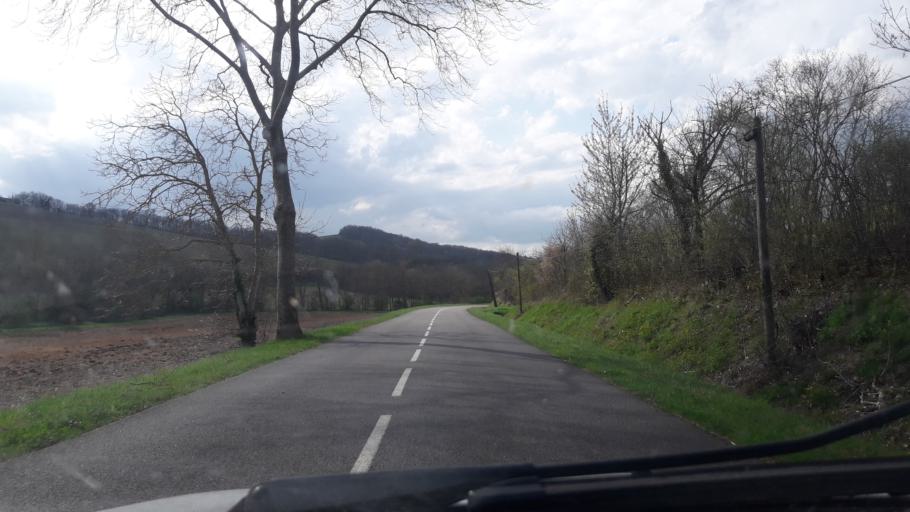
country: FR
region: Midi-Pyrenees
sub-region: Departement de la Haute-Garonne
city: Montesquieu-Volvestre
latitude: 43.2323
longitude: 1.2808
